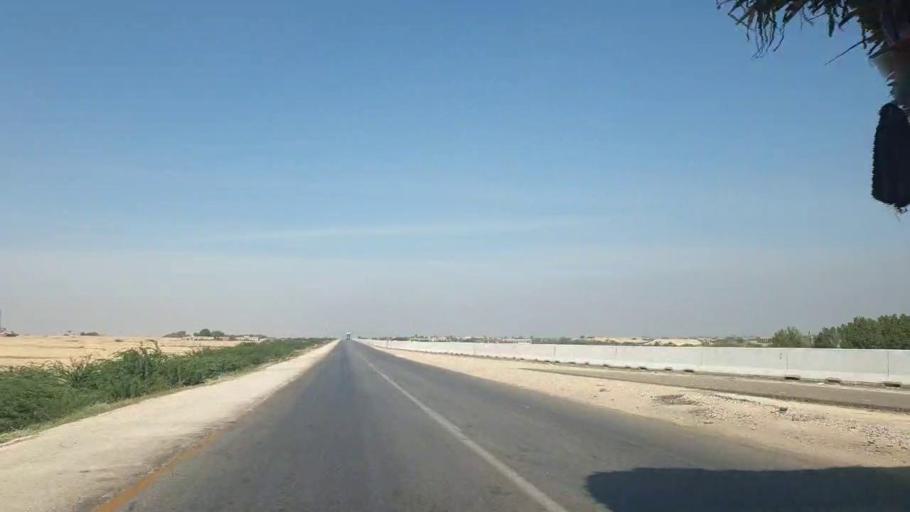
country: PK
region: Sindh
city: Matiari
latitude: 25.6859
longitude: 68.2953
